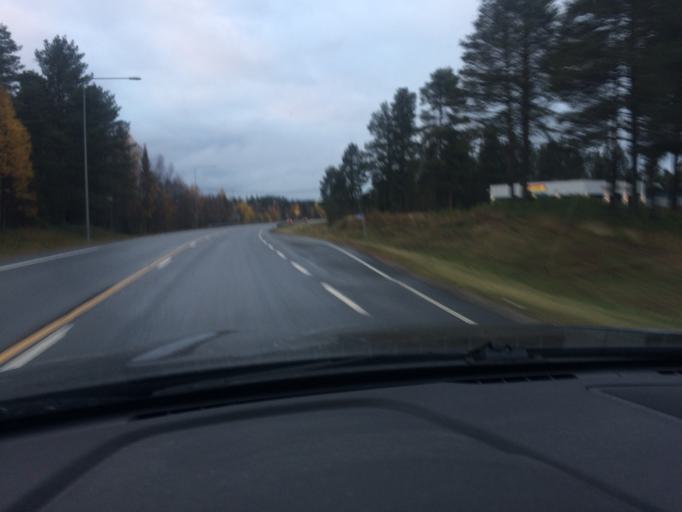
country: FI
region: Northern Ostrobothnia
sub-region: Koillismaa
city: Kuusamo
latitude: 65.9931
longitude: 29.1524
